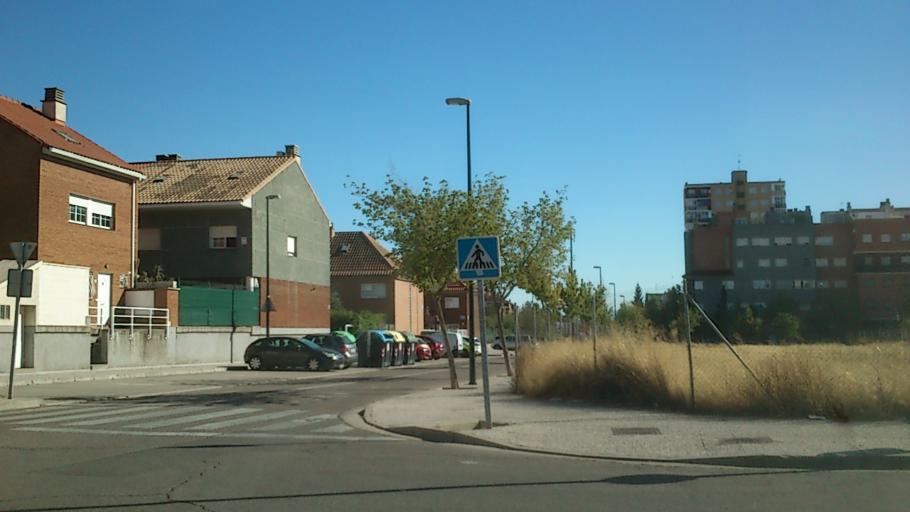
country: ES
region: Aragon
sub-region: Provincia de Zaragoza
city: Zaragoza
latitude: 41.6695
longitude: -0.8233
